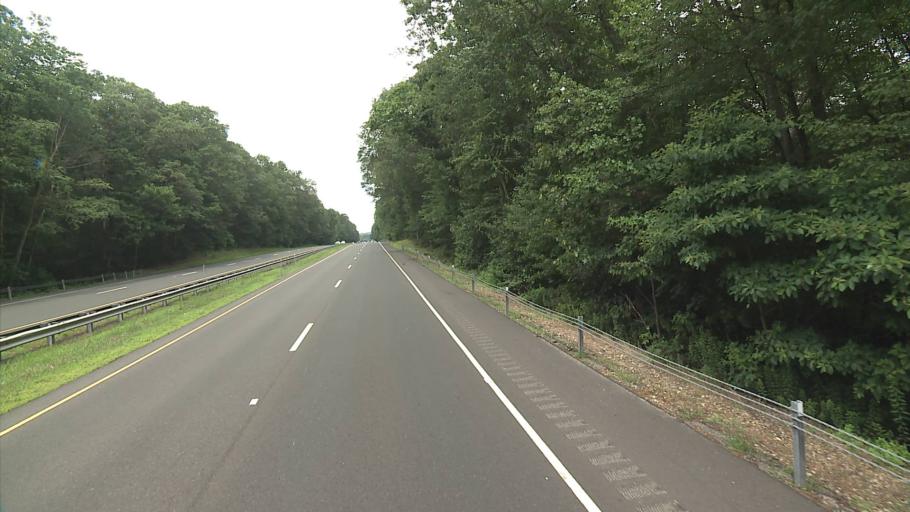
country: US
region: Connecticut
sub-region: New Haven County
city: Madison
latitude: 41.2833
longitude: -72.5661
